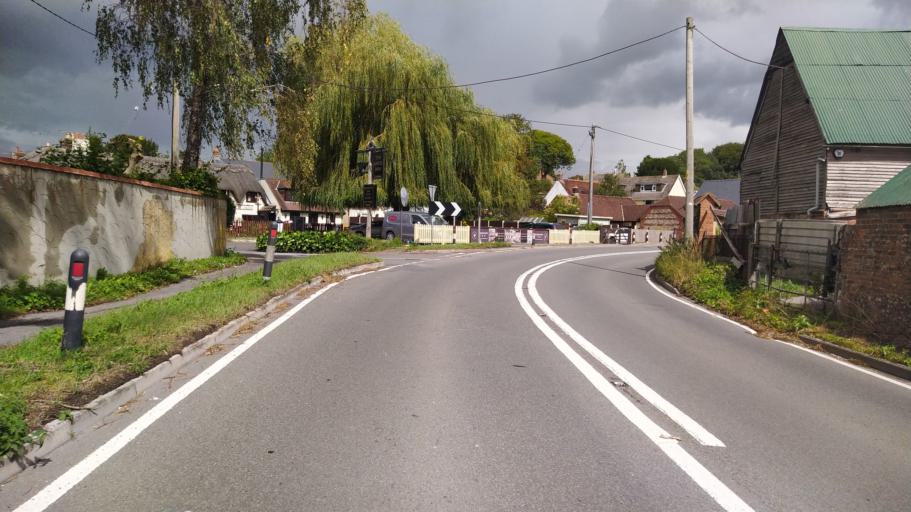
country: GB
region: England
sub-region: Dorset
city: Blandford Forum
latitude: 50.8823
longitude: -2.1345
